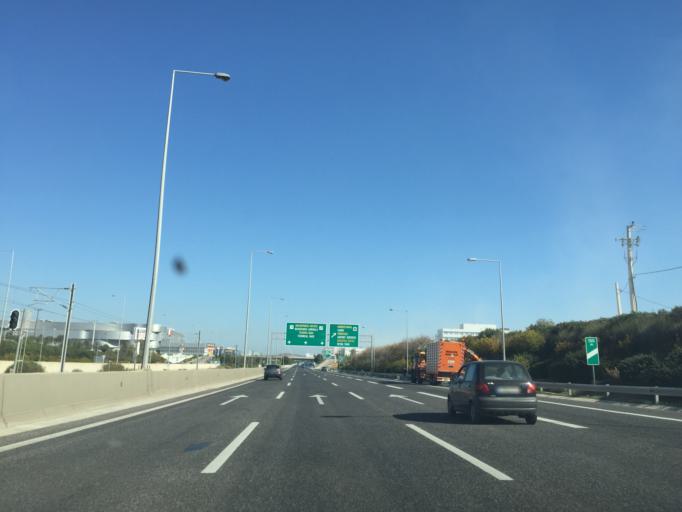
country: GR
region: Attica
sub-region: Nomarchia Anatolikis Attikis
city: Markopoulo
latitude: 37.9177
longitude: 23.9268
